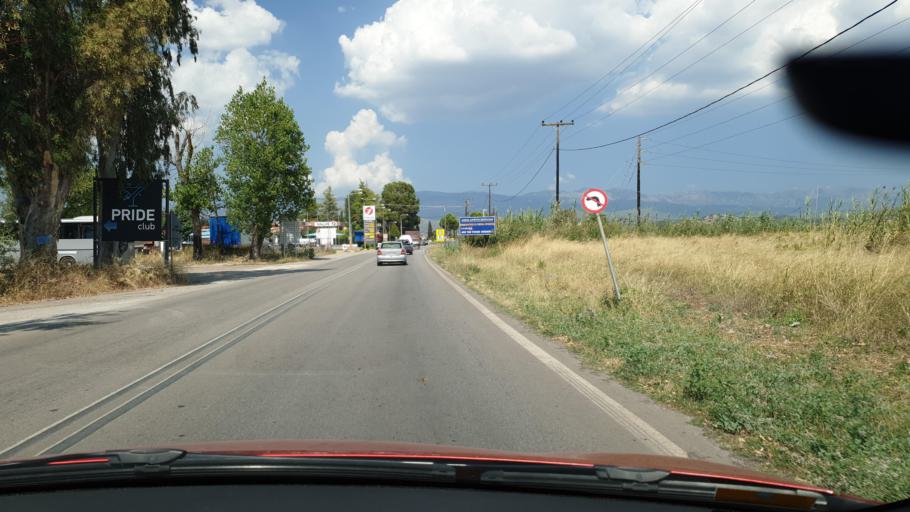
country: GR
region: Central Greece
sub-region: Nomos Evvoias
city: Kastella
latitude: 38.5437
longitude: 23.6270
